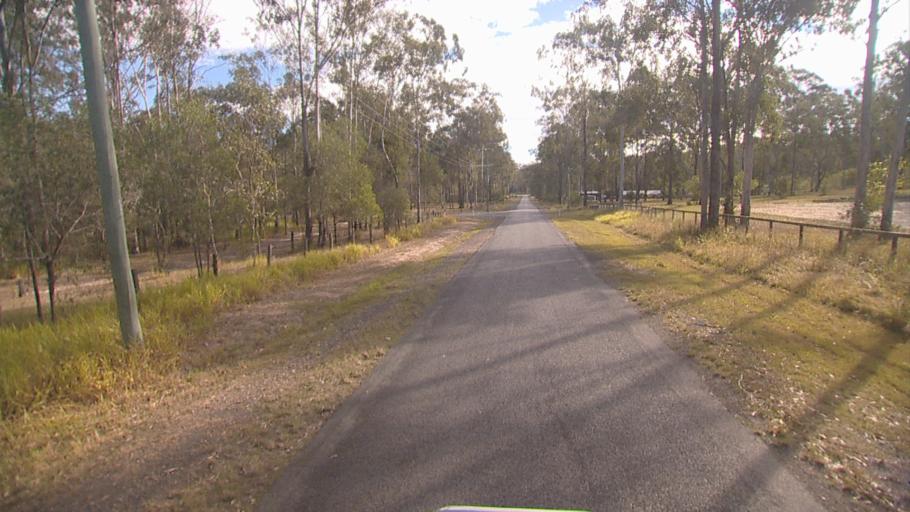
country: AU
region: Queensland
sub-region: Logan
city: Cedar Vale
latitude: -27.8252
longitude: 153.0673
